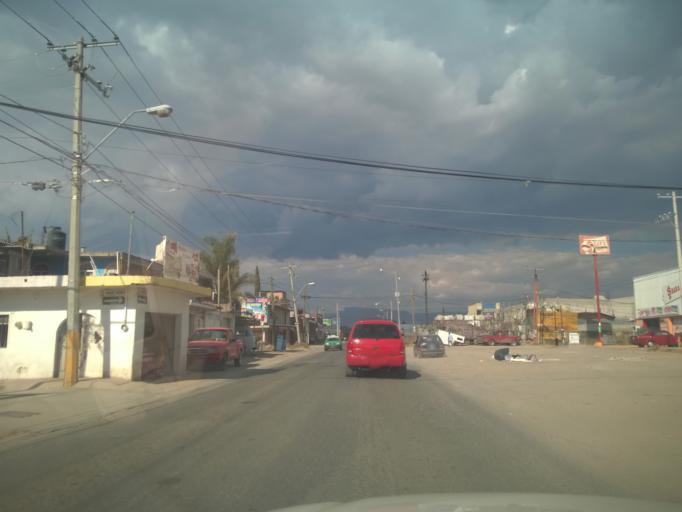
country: MX
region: Guanajuato
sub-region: Leon
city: San Jose de Duran (Los Troncoso)
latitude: 21.0676
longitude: -101.6239
